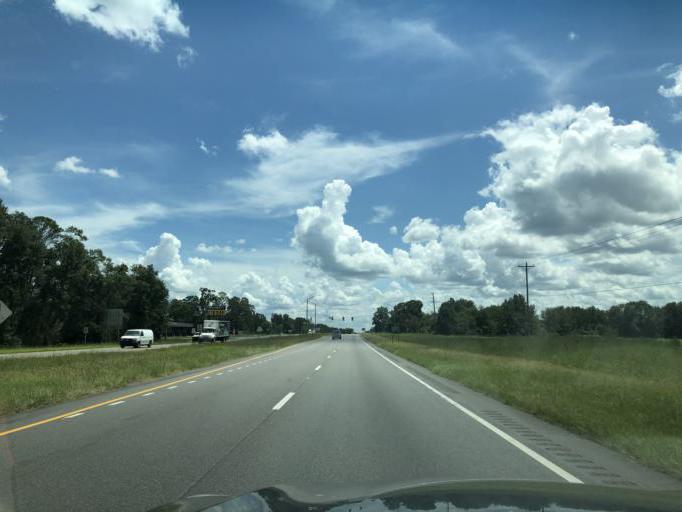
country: US
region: Alabama
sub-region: Houston County
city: Cottonwood
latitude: 31.0013
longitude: -85.4079
